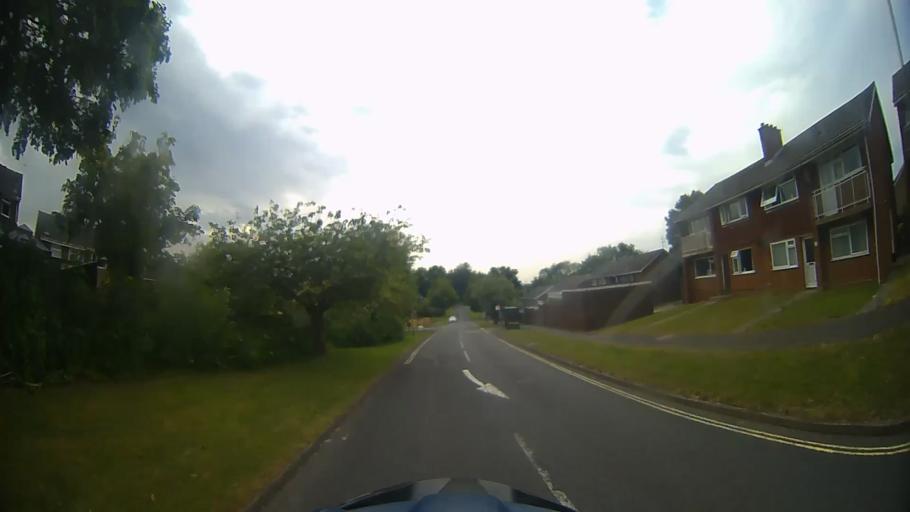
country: GB
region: England
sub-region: Hampshire
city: Basingstoke
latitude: 51.2486
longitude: -1.1051
